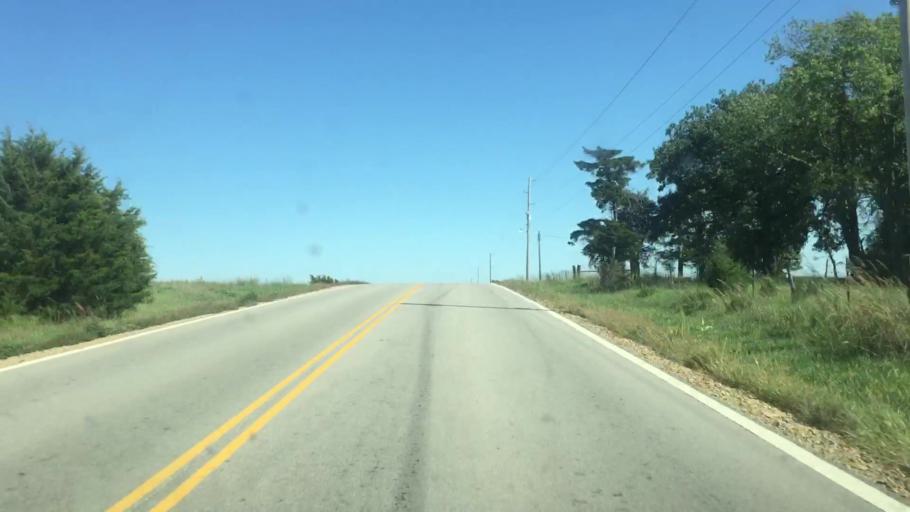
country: US
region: Kansas
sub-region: Jackson County
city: Holton
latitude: 39.5950
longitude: -95.7004
